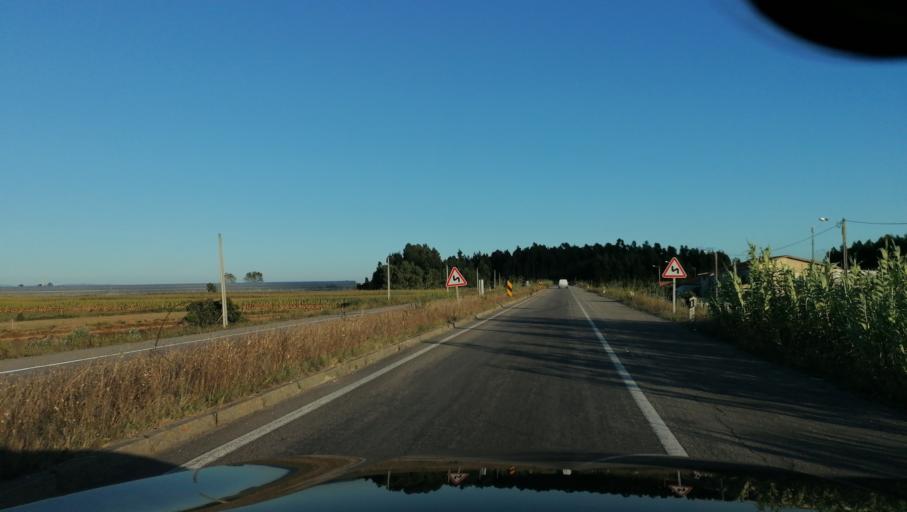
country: PT
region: Aveiro
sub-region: Aveiro
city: Oliveirinha
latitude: 40.6004
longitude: -8.6172
